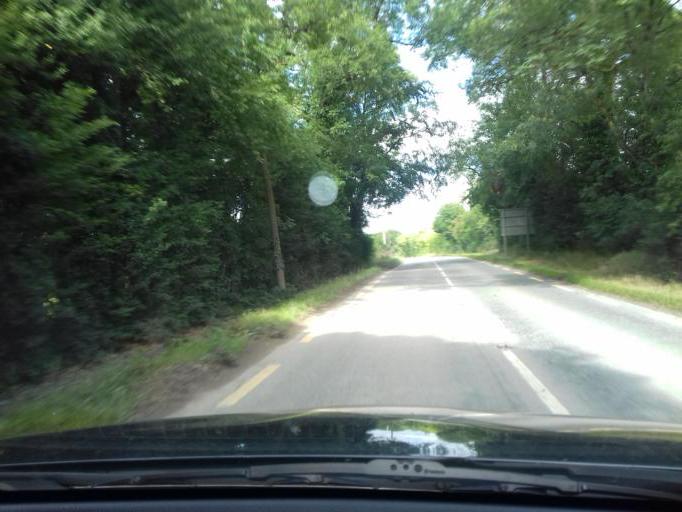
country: IE
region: Leinster
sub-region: Wicklow
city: Baltinglass
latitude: 52.9983
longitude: -6.6463
